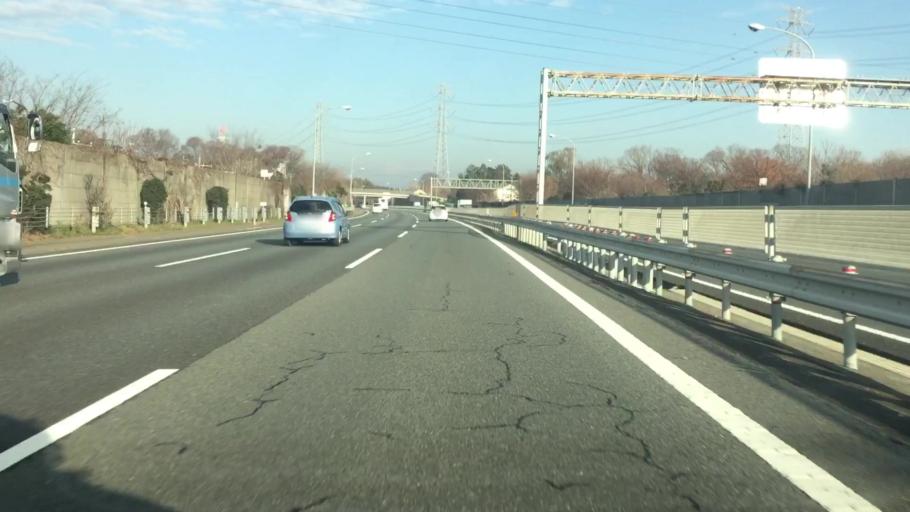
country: JP
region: Saitama
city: Sakado
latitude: 36.0306
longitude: 139.3805
